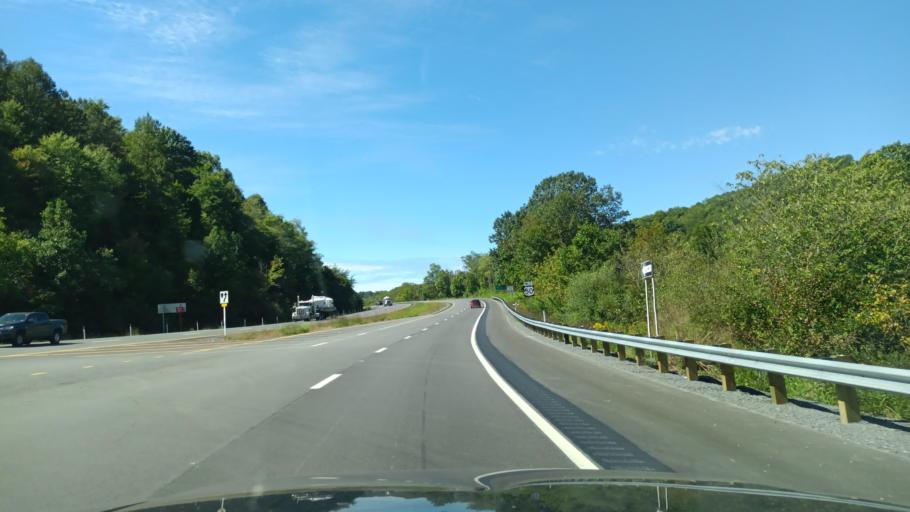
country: US
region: West Virginia
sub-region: Harrison County
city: Clarksburg
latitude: 39.2817
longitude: -80.4515
